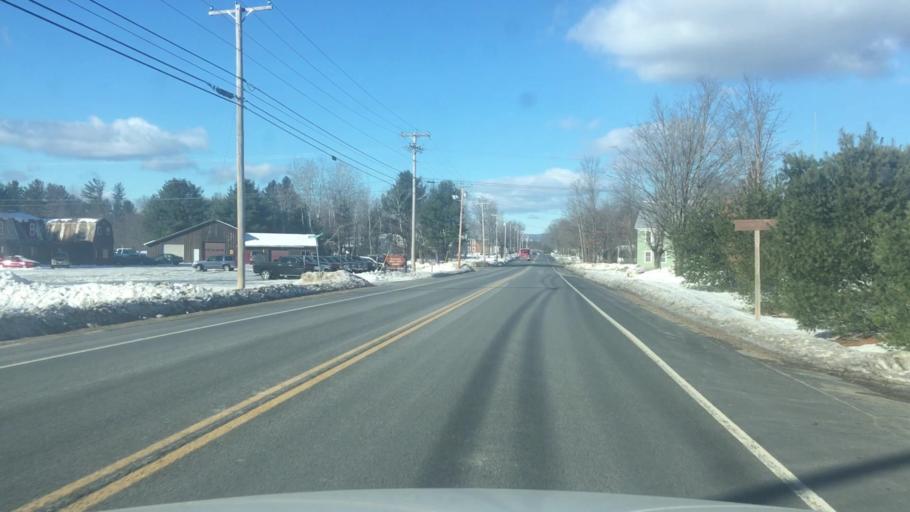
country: US
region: Maine
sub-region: Somerset County
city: Madison
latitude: 44.9459
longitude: -69.8539
